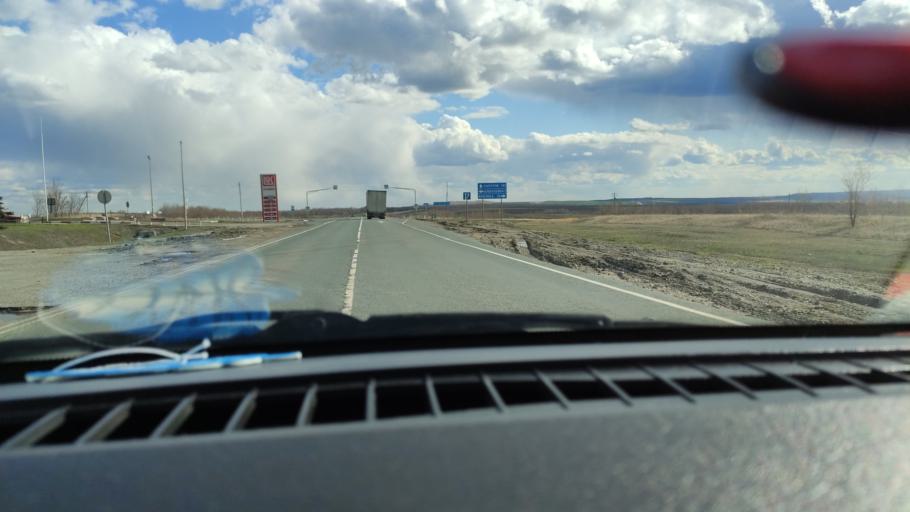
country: RU
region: Saratov
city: Alekseyevka
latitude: 52.2905
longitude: 47.9298
